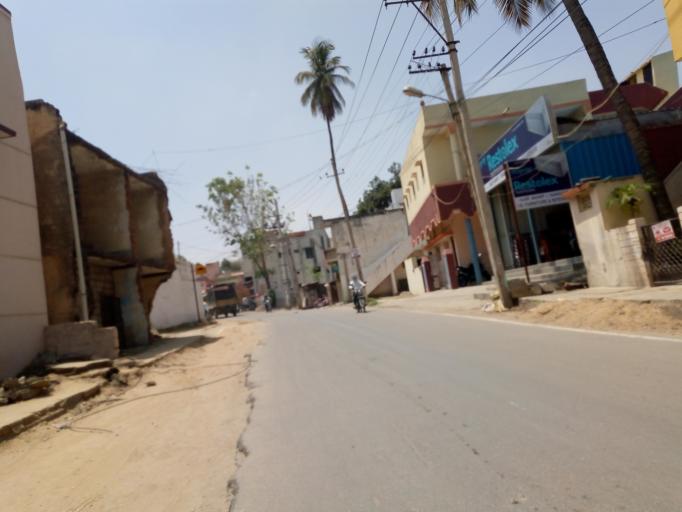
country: IN
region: Karnataka
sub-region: Bangalore Urban
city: Bangalore
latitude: 12.8903
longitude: 77.6563
